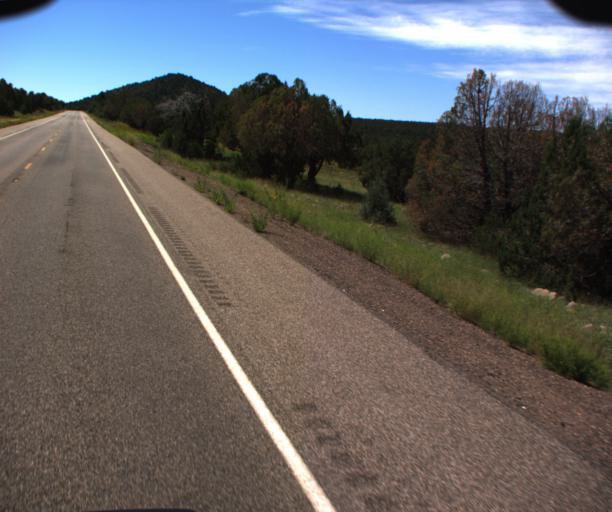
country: US
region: Arizona
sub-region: Gila County
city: San Carlos
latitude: 33.6662
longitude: -110.5723
